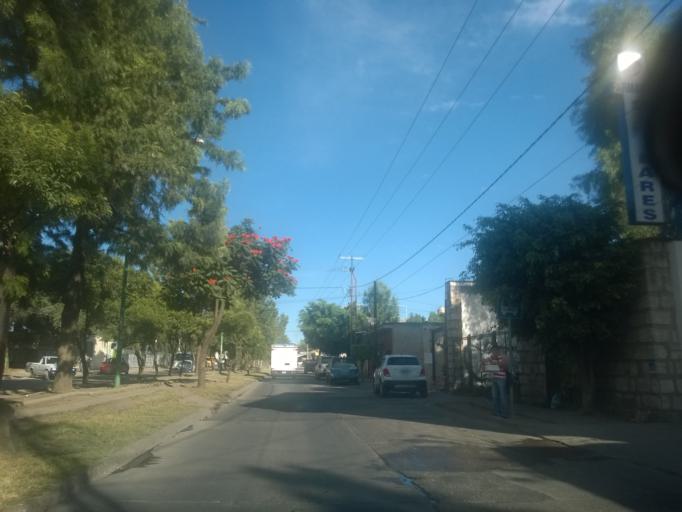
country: MX
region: Guanajuato
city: Leon
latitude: 21.1189
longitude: -101.6470
